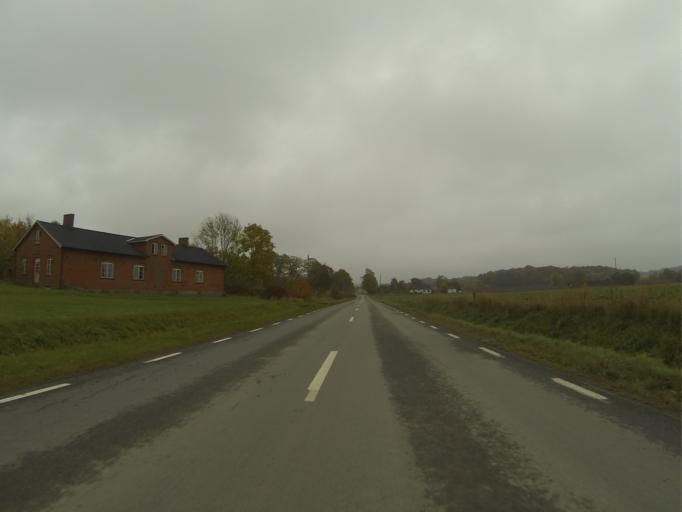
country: SE
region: Skane
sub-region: Tomelilla Kommun
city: Tomelilla
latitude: 55.6087
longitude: 13.9283
